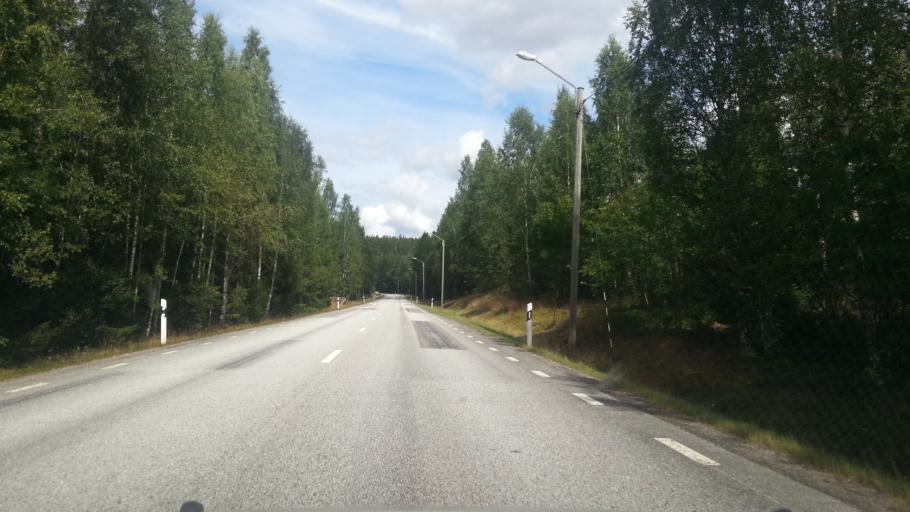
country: SE
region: Vaestmanland
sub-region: Skinnskattebergs Kommun
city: Skinnskatteberg
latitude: 59.8169
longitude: 15.5302
